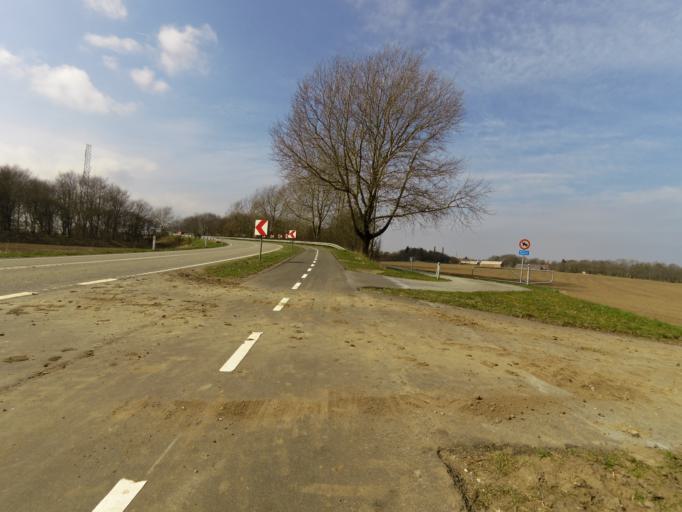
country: DK
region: Central Jutland
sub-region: Struer Kommune
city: Struer
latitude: 56.4764
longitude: 8.6143
